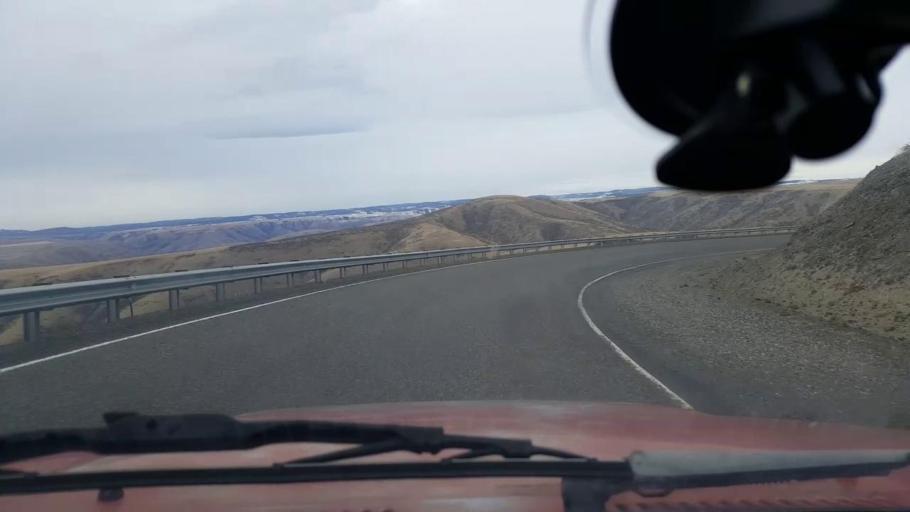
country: US
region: Washington
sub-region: Asotin County
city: Clarkston Heights-Vineland
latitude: 46.3345
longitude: -117.2812
